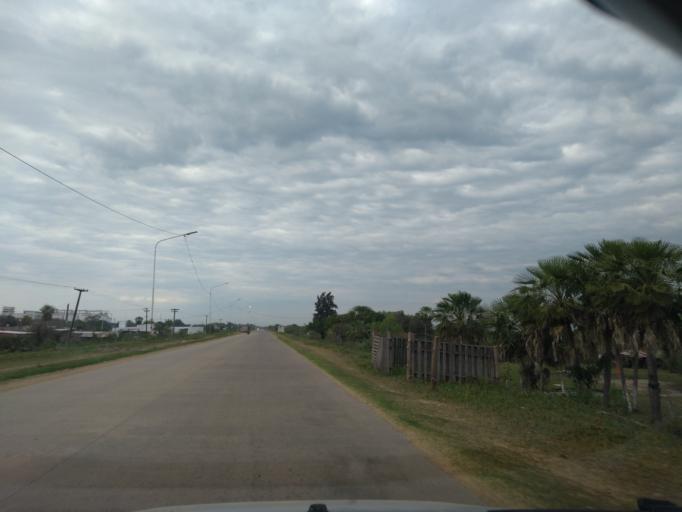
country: AR
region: Chaco
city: Puerto Vilelas
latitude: -27.5284
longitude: -58.9322
